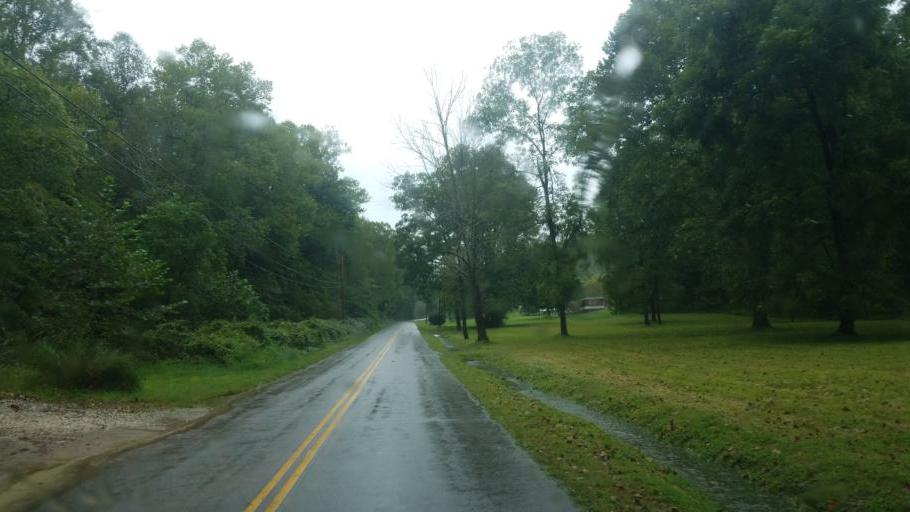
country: US
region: Ohio
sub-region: Scioto County
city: West Portsmouth
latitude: 38.7447
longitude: -83.0828
